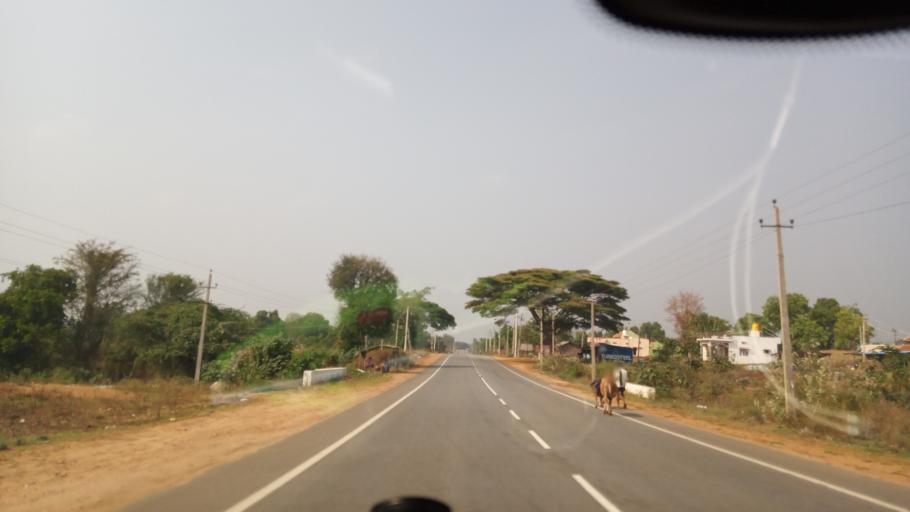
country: IN
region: Karnataka
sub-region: Mandya
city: Melukote
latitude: 12.7019
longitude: 76.6997
